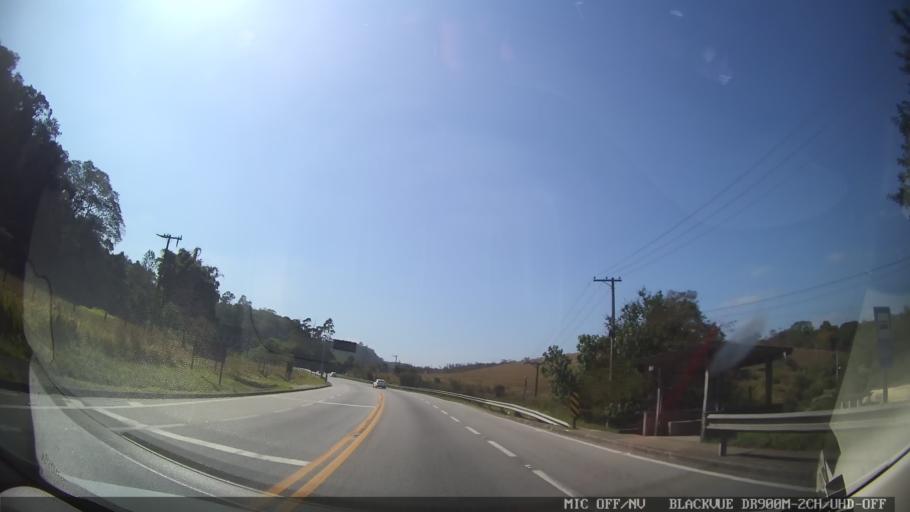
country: BR
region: Sao Paulo
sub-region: Francisco Morato
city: Francisco Morato
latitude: -23.2857
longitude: -46.7977
